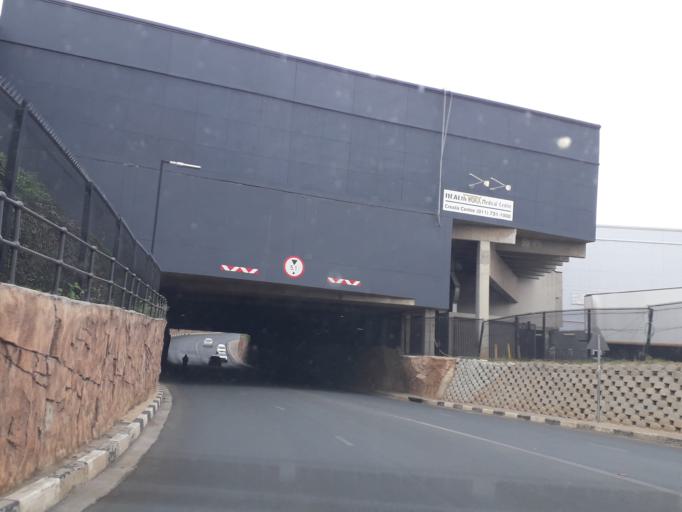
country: ZA
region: Gauteng
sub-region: City of Johannesburg Metropolitan Municipality
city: Johannesburg
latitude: -26.1299
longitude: 27.9756
